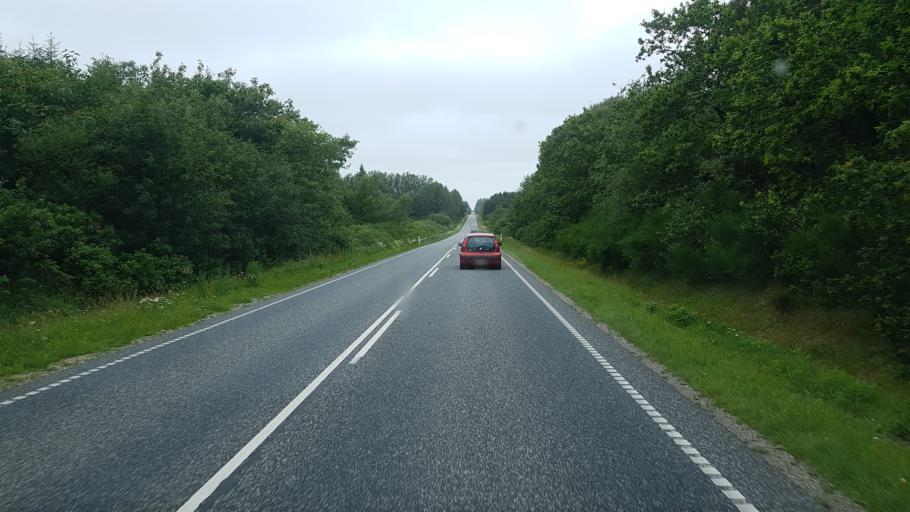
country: DK
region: Central Jutland
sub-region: Lemvig Kommune
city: Lemvig
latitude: 56.4565
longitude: 8.3379
